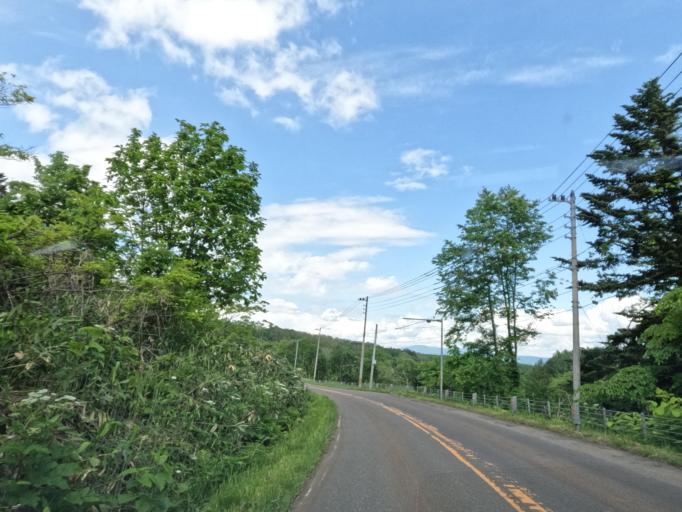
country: JP
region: Hokkaido
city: Takikawa
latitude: 43.5761
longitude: 141.8376
